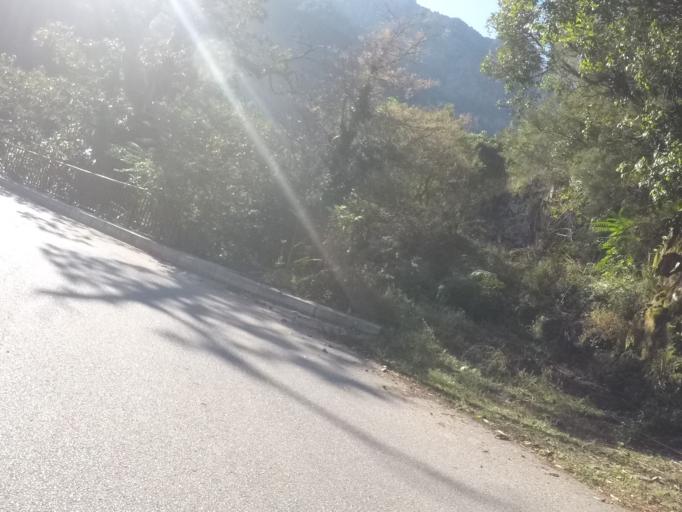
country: FR
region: Corsica
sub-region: Departement de la Corse-du-Sud
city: Cargese
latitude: 42.2415
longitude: 8.7321
